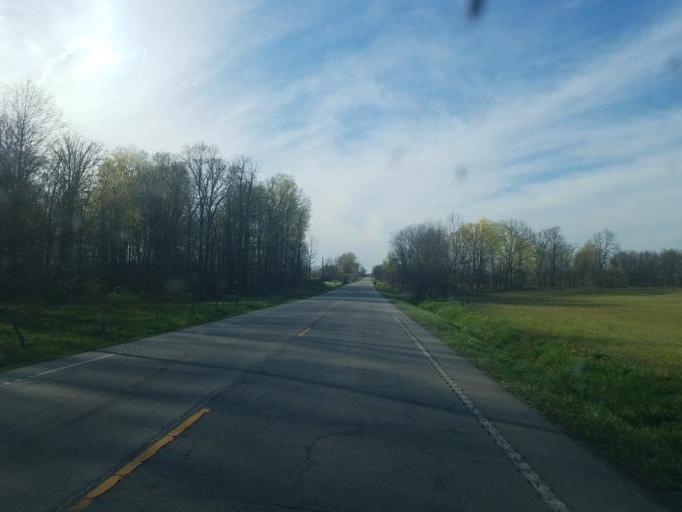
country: US
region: Ohio
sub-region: Huron County
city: New London
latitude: 41.0398
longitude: -82.4273
